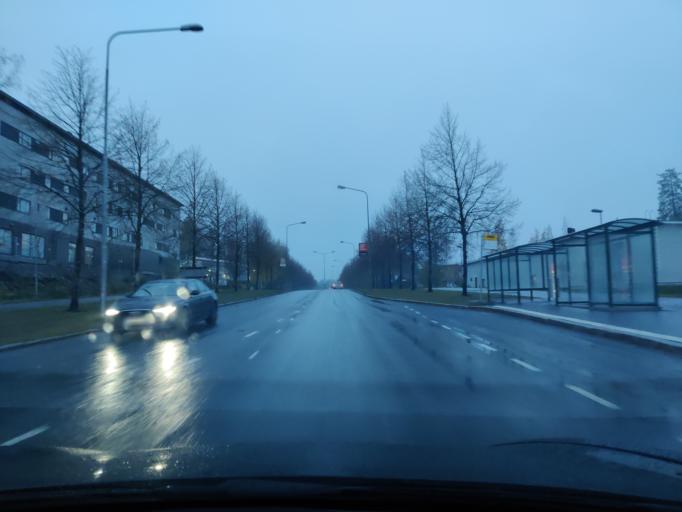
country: FI
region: Northern Savo
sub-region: Kuopio
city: Kuopio
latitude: 62.8343
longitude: 27.6658
